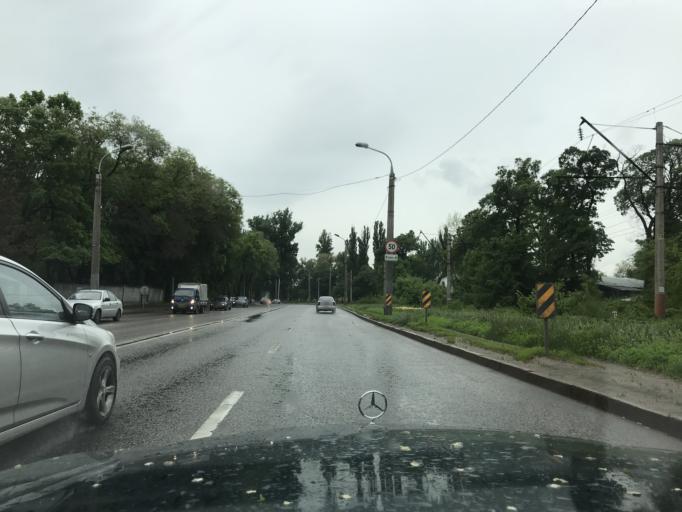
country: KZ
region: Almaty Qalasy
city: Almaty
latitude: 43.2937
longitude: 76.9476
